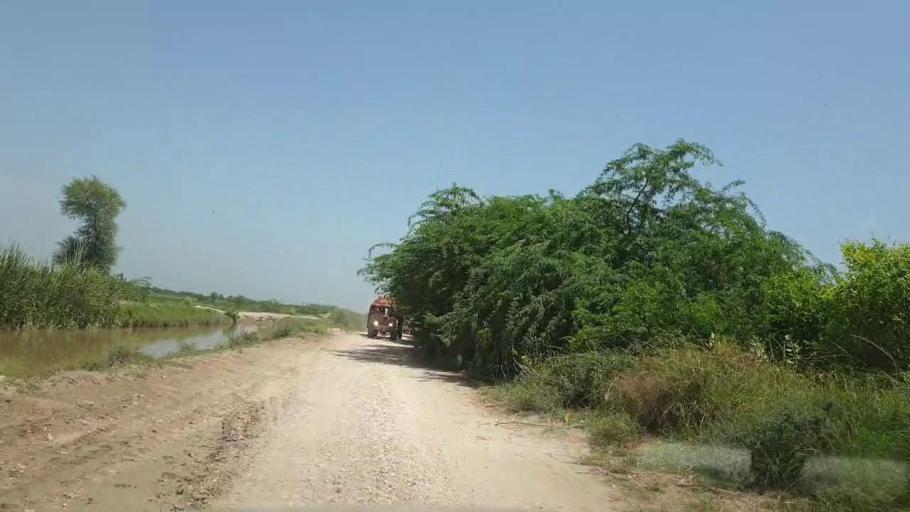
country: PK
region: Sindh
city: Rohri
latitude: 27.6338
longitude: 69.1004
